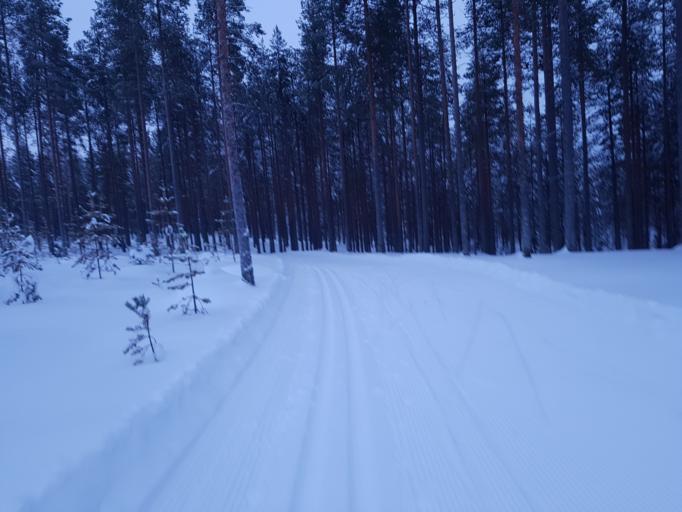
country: FI
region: Kainuu
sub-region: Kehys-Kainuu
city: Kuhmo
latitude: 64.0856
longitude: 29.5180
